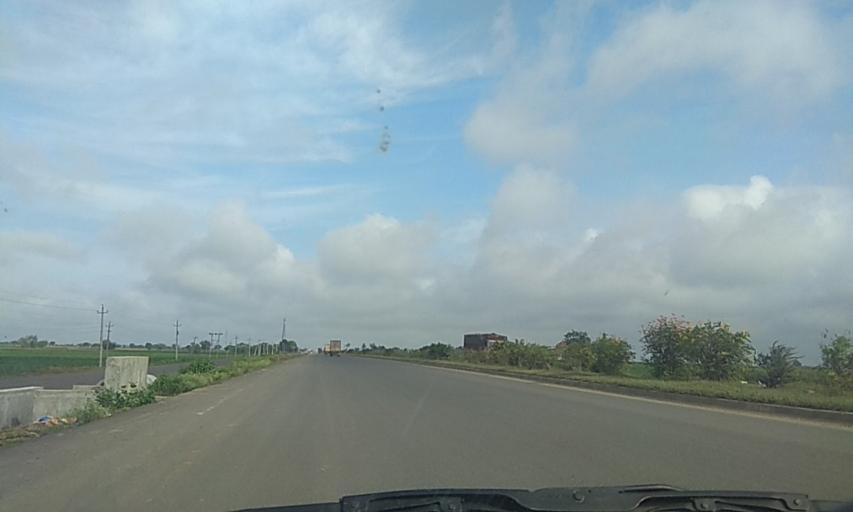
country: IN
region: Karnataka
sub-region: Haveri
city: Savanur
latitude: 14.8745
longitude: 75.3161
